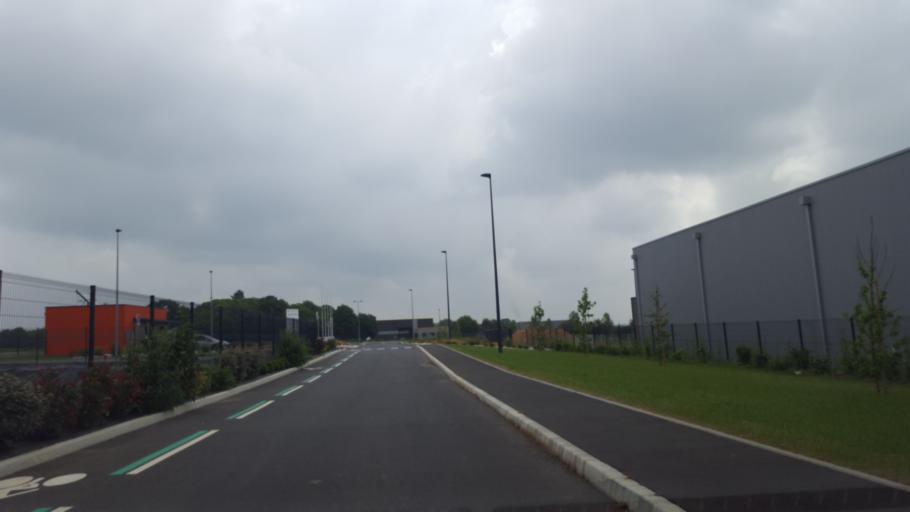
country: FR
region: Brittany
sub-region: Departement d'Ille-et-Vilaine
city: Grand-Fougeray
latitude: 47.7481
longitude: -1.7220
